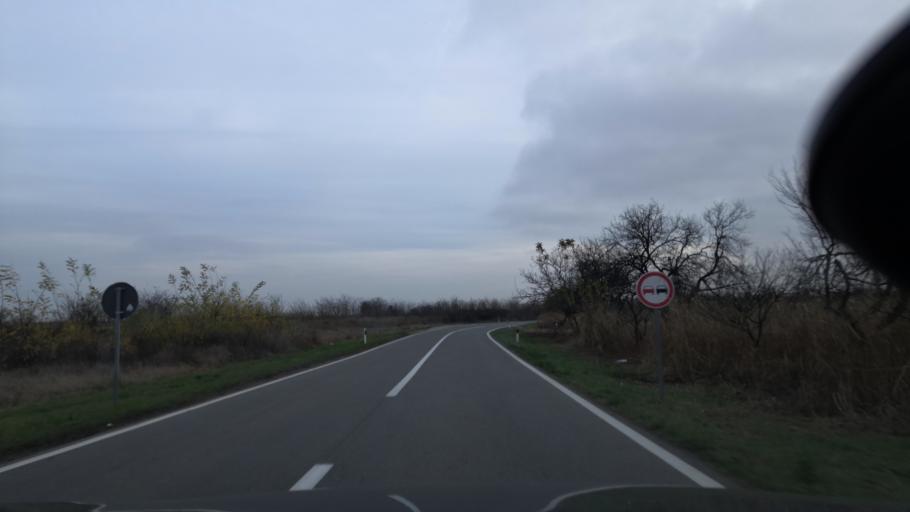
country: RS
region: Autonomna Pokrajina Vojvodina
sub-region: Severnobanatski Okrug
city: Coka
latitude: 45.9626
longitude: 20.1317
